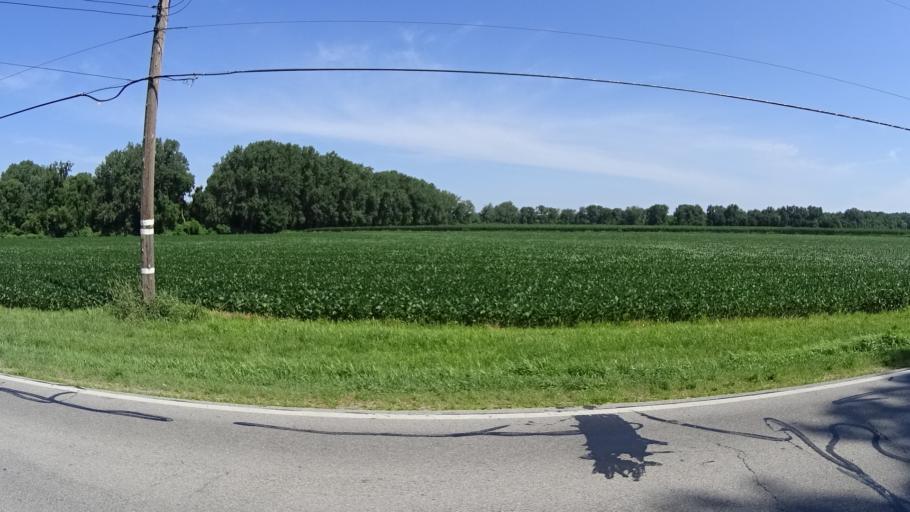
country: US
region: Ohio
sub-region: Huron County
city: Bellevue
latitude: 41.3920
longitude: -82.8251
